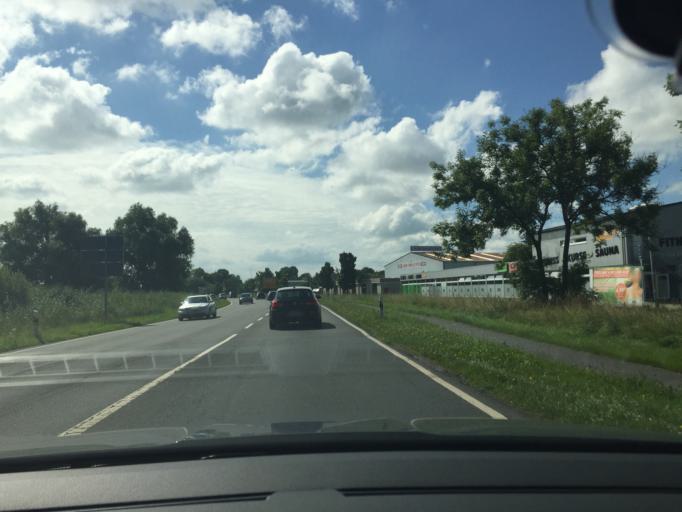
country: DE
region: Lower Saxony
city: Wilhelmshaven
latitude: 53.5263
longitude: 8.0696
